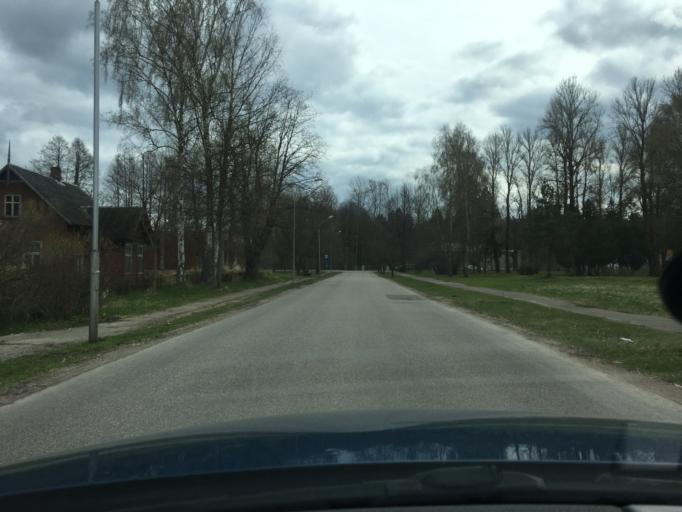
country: LV
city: Tireli
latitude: 56.9427
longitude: 23.4912
